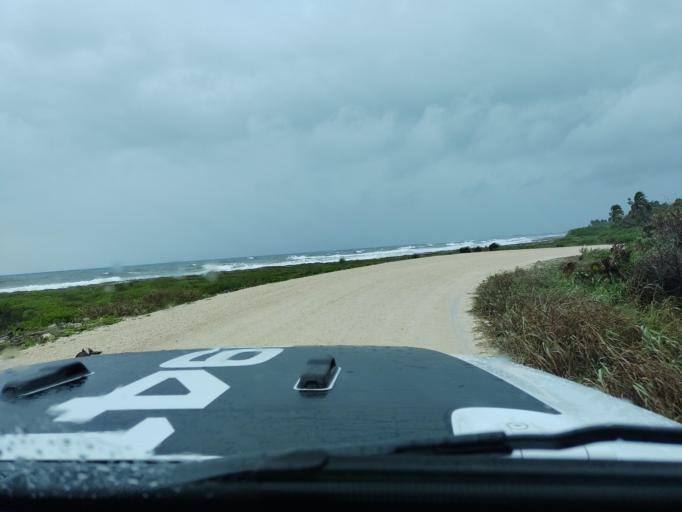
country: MX
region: Quintana Roo
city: Tulum
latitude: 19.9914
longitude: -87.4643
